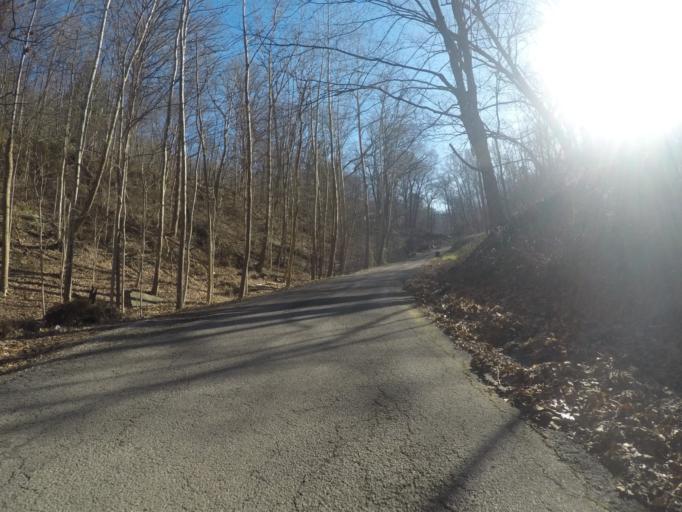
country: US
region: Ohio
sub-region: Lawrence County
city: Burlington
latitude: 38.3967
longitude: -82.4992
